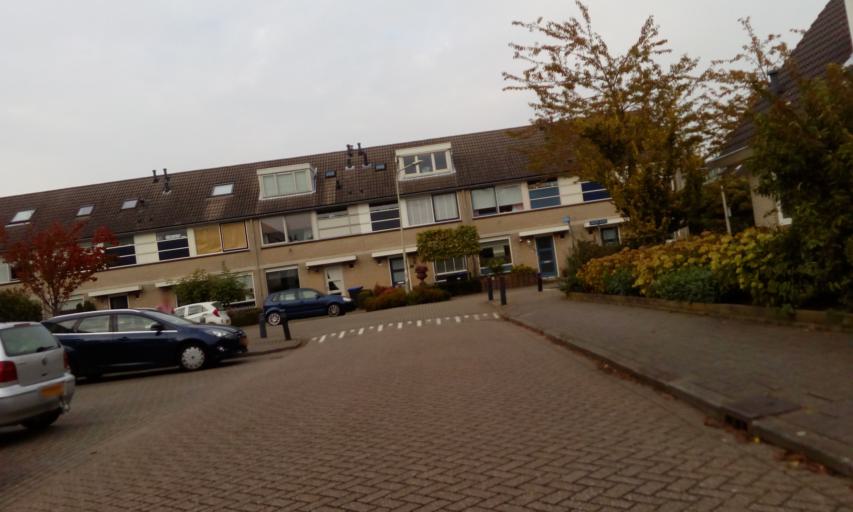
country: NL
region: South Holland
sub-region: Gemeente Lansingerland
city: Bleiswijk
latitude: 52.0109
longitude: 4.5472
